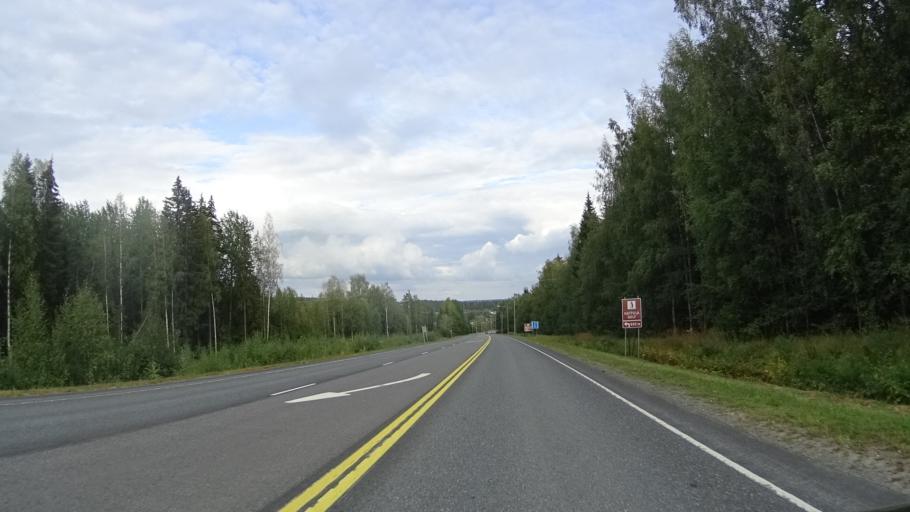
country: FI
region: Haeme
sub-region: Haemeenlinna
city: Parola
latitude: 61.0254
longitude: 24.3107
